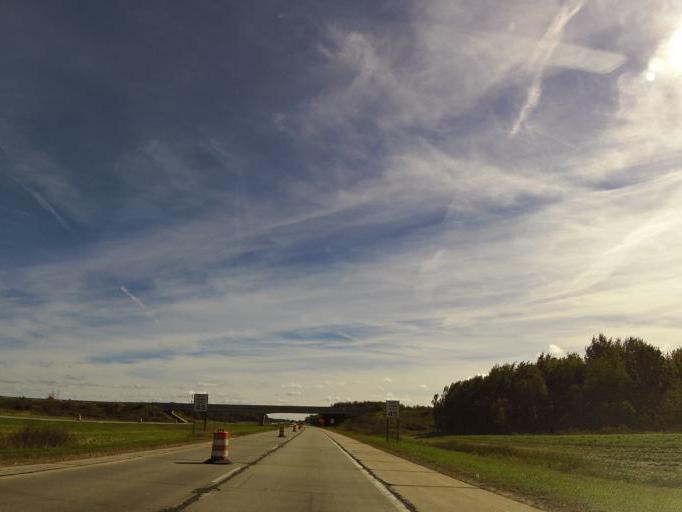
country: US
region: Michigan
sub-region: Macomb County
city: Memphis
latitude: 42.9783
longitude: -82.7874
